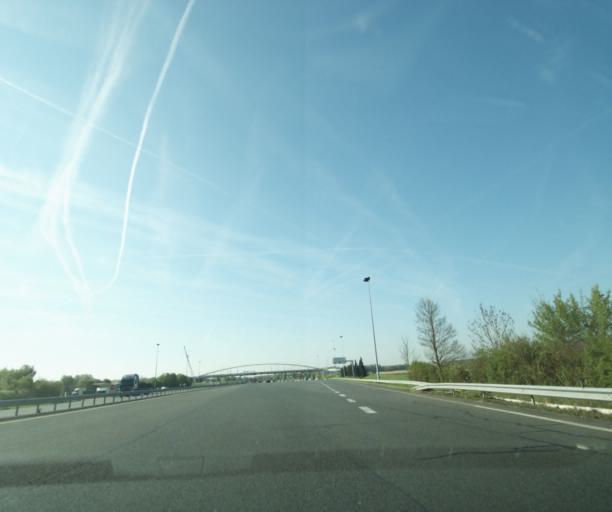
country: FR
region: Ile-de-France
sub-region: Departement de Seine-et-Marne
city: Souppes-sur-Loing
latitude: 48.1789
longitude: 2.7668
